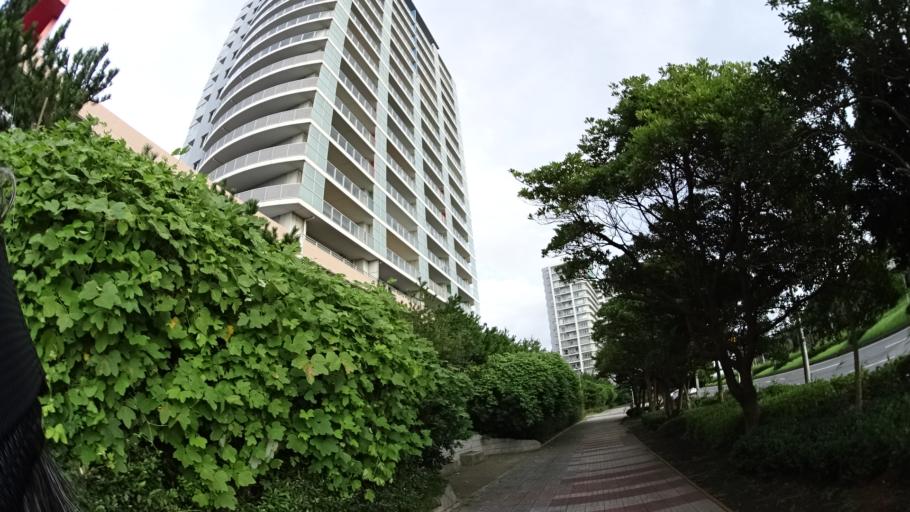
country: JP
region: Chiba
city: Funabashi
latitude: 35.6414
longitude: 140.0389
